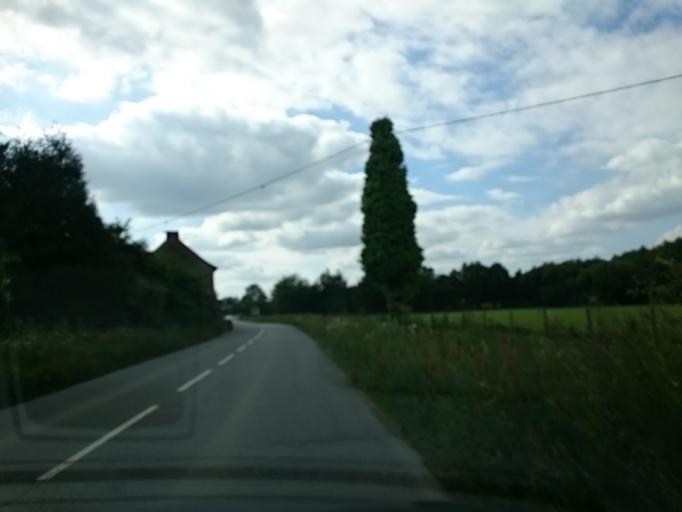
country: FR
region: Brittany
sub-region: Departement d'Ille-et-Vilaine
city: Laille
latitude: 47.9768
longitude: -1.7059
